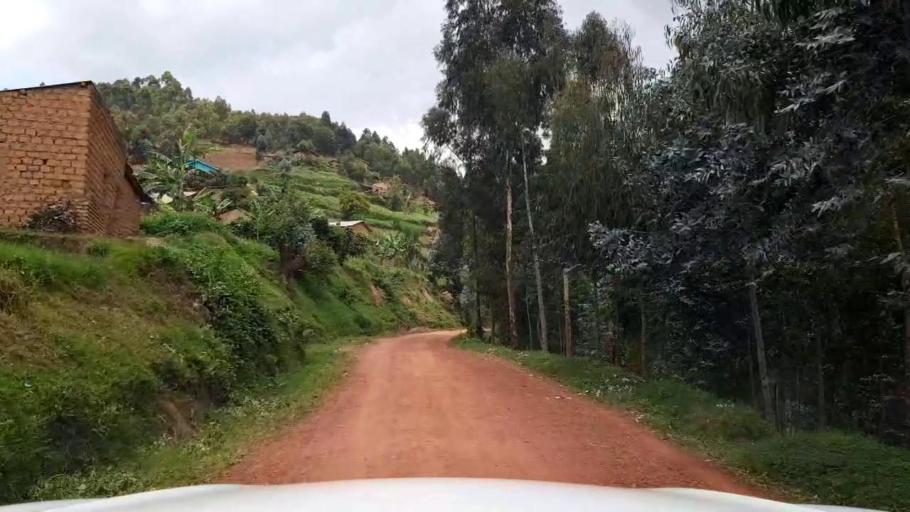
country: RW
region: Northern Province
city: Byumba
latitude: -1.4834
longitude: 29.9205
